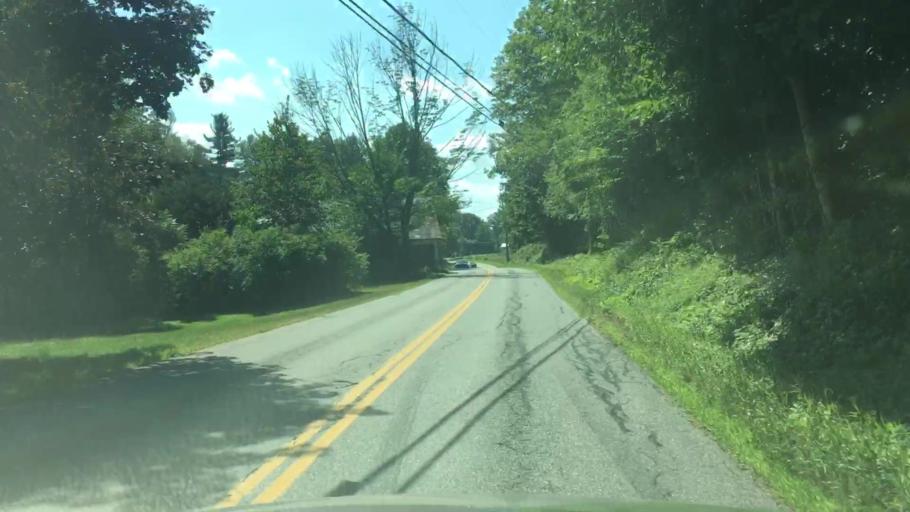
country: US
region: Vermont
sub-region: Windham County
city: West Brattleboro
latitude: 42.7882
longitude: -72.5993
